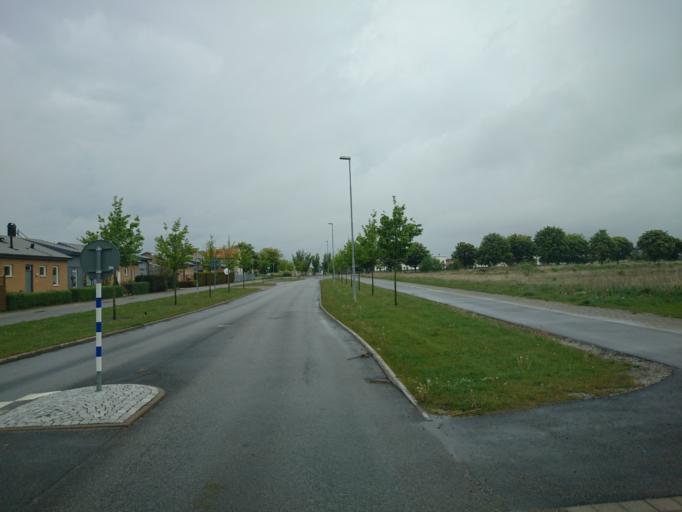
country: SE
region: Skane
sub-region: Malmo
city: Bunkeflostrand
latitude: 55.5527
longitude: 12.9286
